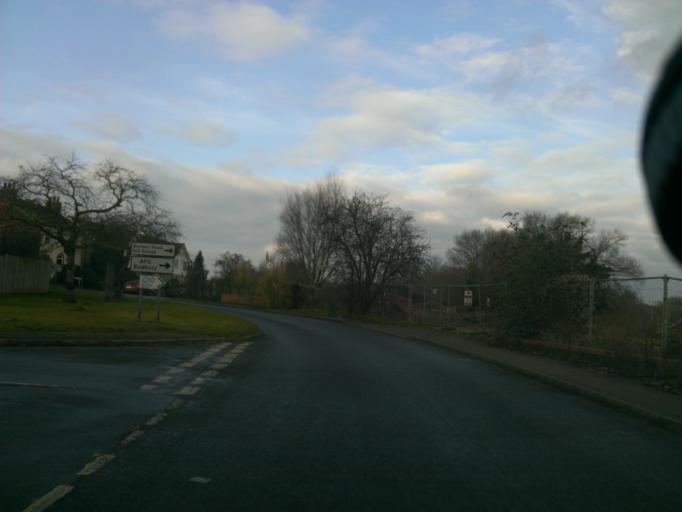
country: GB
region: England
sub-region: Suffolk
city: Sudbury
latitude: 52.0344
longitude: 0.7145
